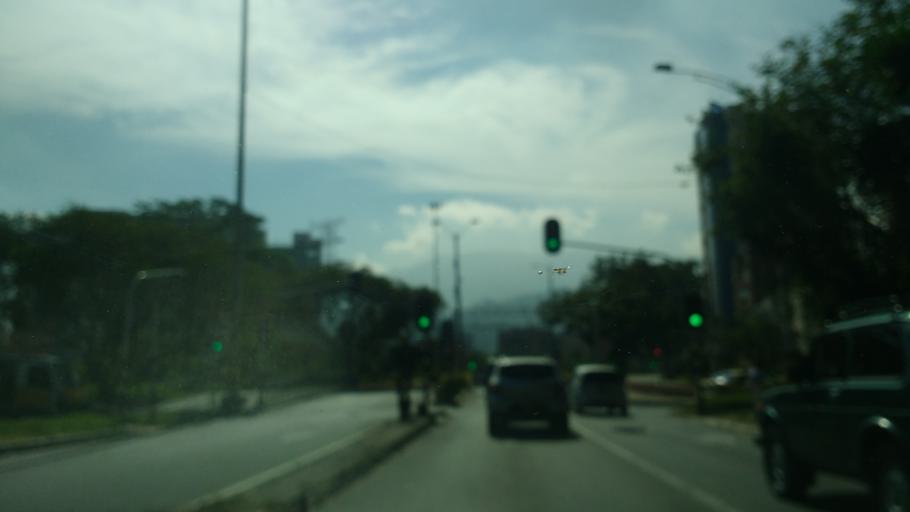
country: CO
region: Antioquia
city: Medellin
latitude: 6.2460
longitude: -75.5813
